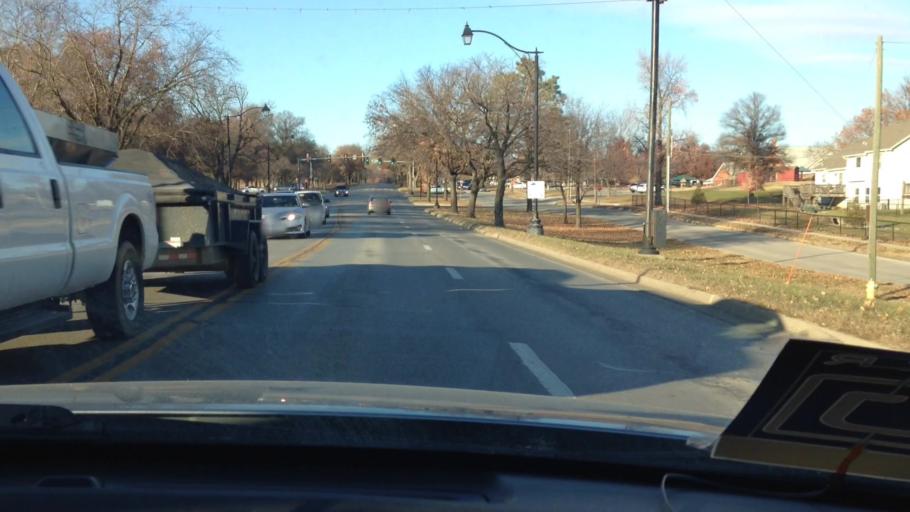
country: US
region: Kansas
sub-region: Leavenworth County
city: Leavenworth
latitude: 39.3364
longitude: -94.9216
